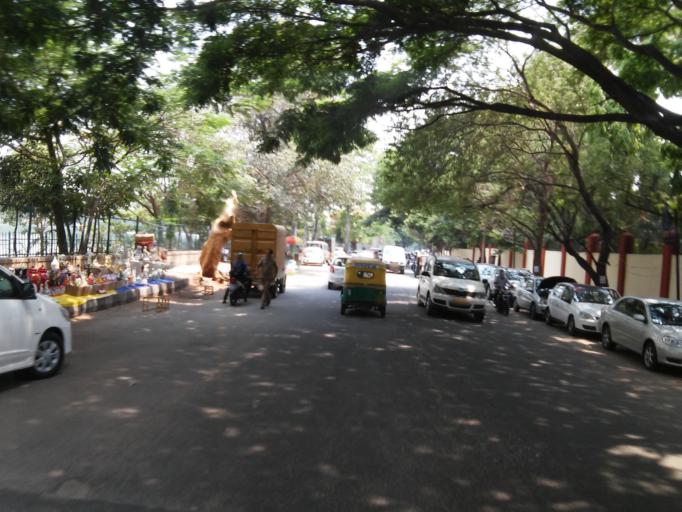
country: IN
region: Karnataka
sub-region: Bangalore Urban
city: Bangalore
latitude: 12.9860
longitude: 77.6193
